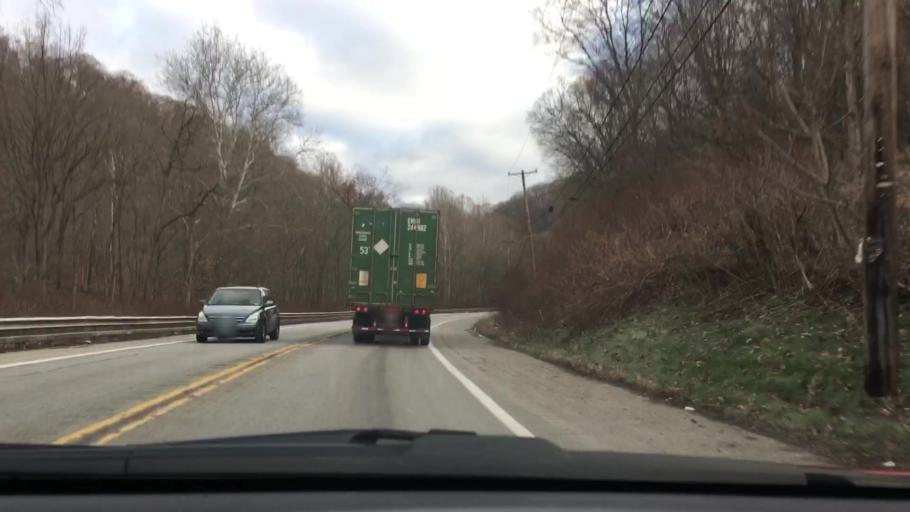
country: US
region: Pennsylvania
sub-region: Allegheny County
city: Pitcairn
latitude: 40.4020
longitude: -79.7657
